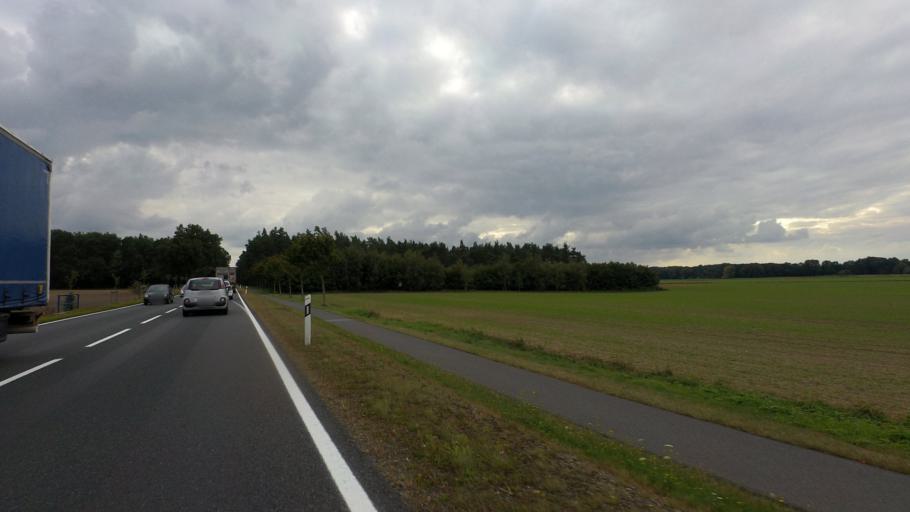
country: DE
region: Saxony
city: Neschwitz
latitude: 51.2889
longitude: 14.3297
